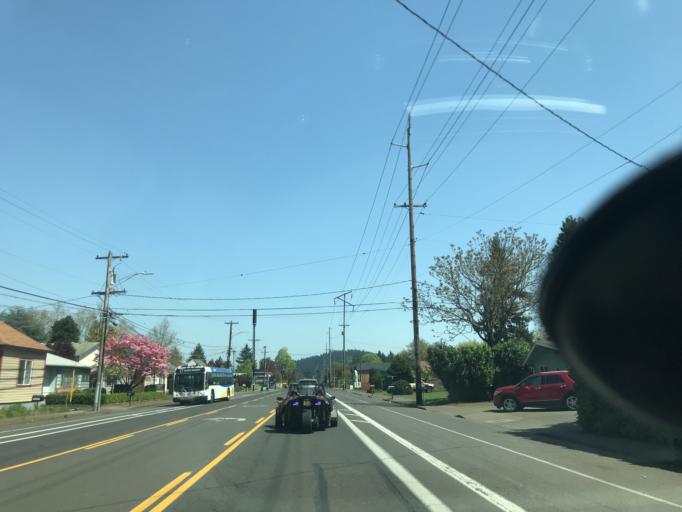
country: US
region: Oregon
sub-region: Multnomah County
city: Lents
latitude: 45.4897
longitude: -122.5507
